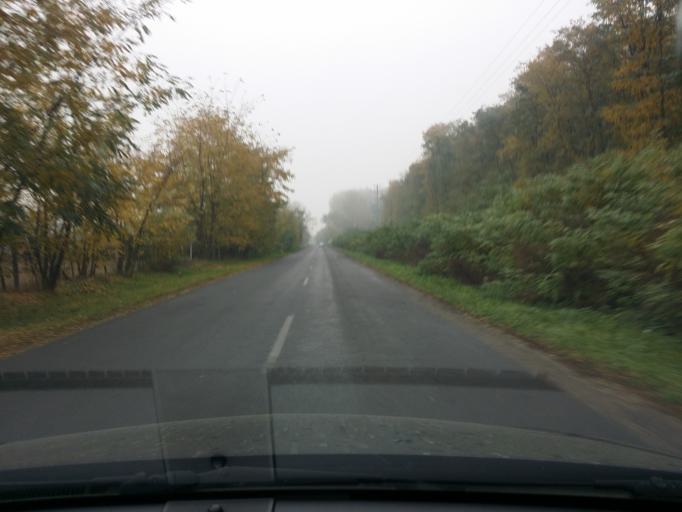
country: HU
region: Szabolcs-Szatmar-Bereg
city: Kek
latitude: 48.0942
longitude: 21.8790
